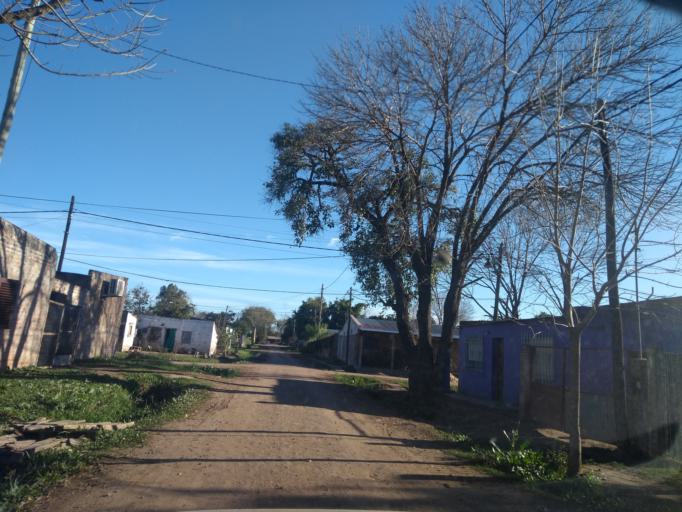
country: AR
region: Chaco
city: Barranqueras
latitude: -27.4730
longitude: -58.9279
